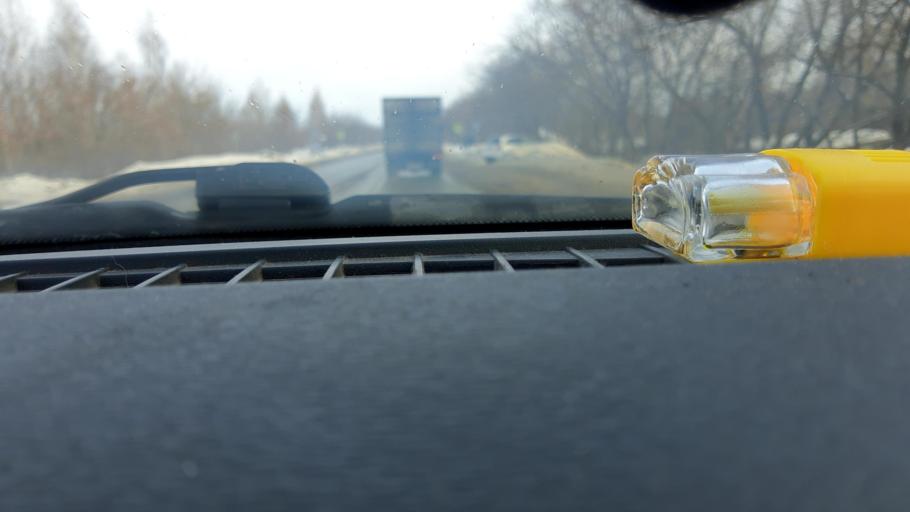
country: RU
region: Bashkortostan
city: Iglino
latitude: 54.7748
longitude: 56.2490
